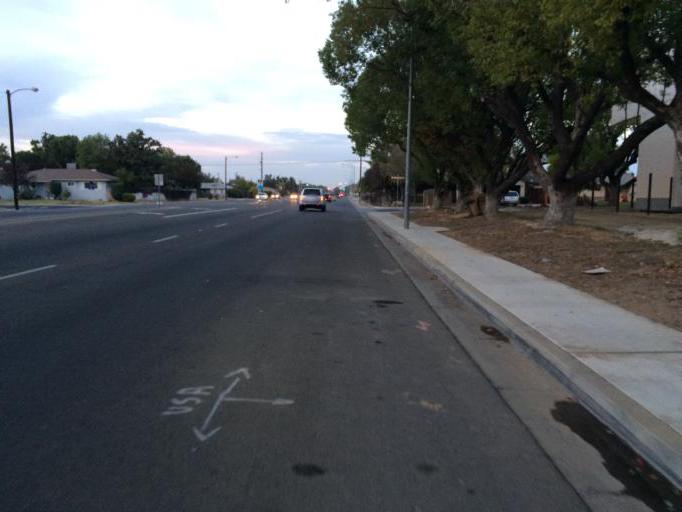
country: US
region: California
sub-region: Fresno County
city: Tarpey Village
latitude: 36.8037
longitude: -119.7271
